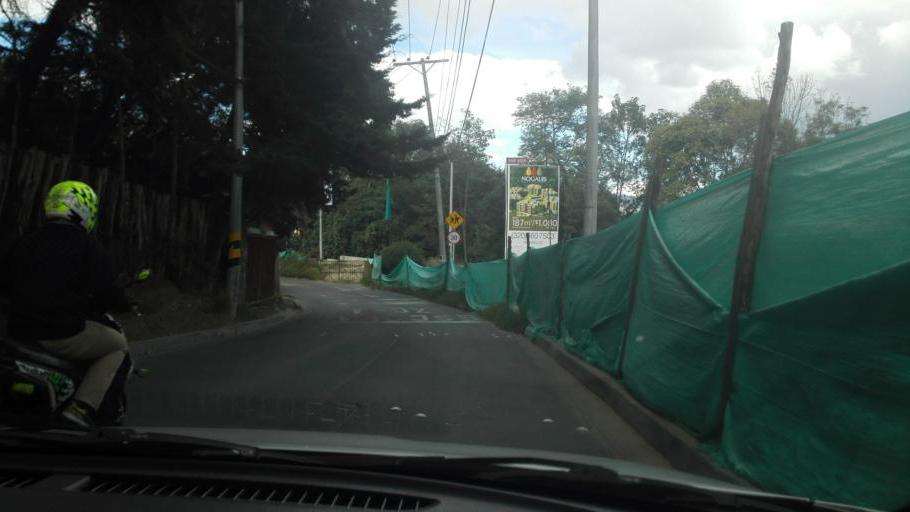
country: CO
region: Cundinamarca
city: Cota
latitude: 4.7409
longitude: -74.0729
